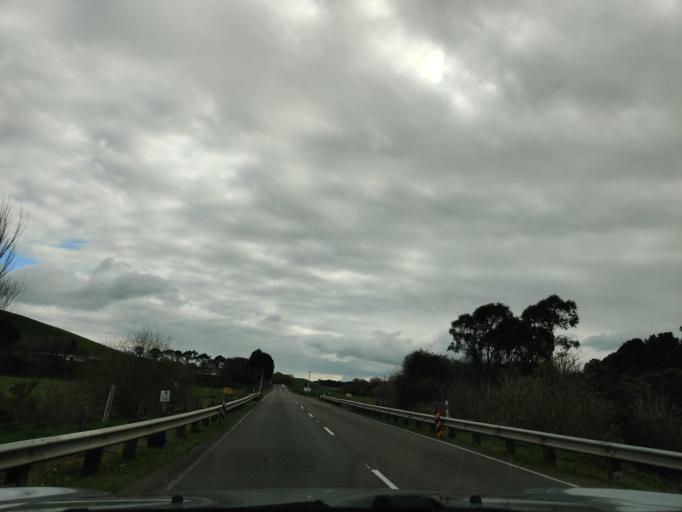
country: NZ
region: Manawatu-Wanganui
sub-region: Palmerston North City
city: Palmerston North
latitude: -40.2818
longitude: 175.9886
